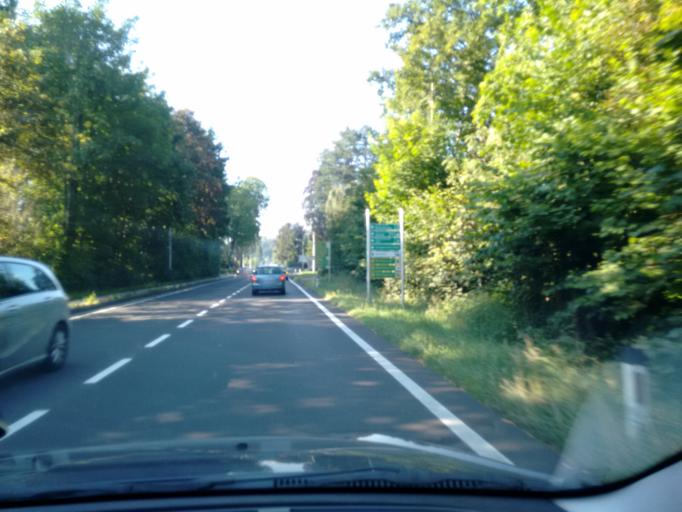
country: AT
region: Upper Austria
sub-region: Politischer Bezirk Gmunden
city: Altmunster
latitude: 47.8969
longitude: 13.7652
